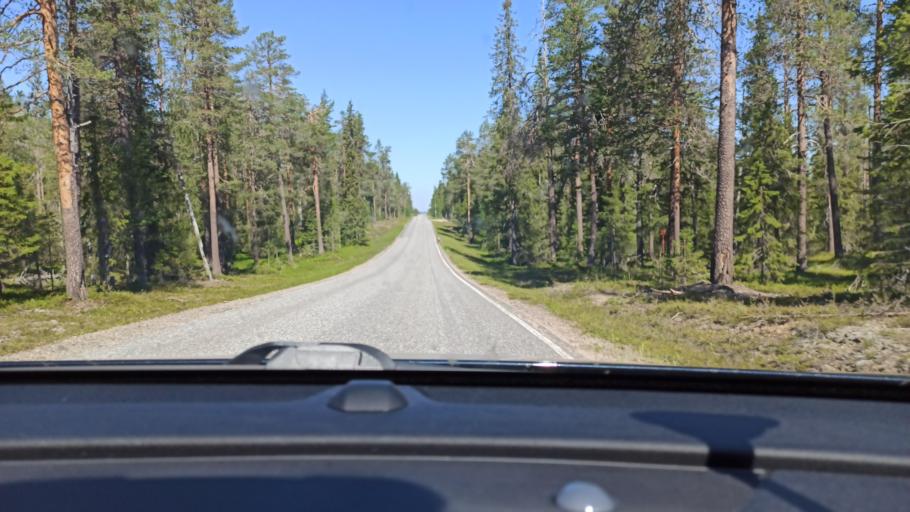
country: FI
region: Lapland
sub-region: Tunturi-Lappi
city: Kolari
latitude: 67.6716
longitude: 24.1491
